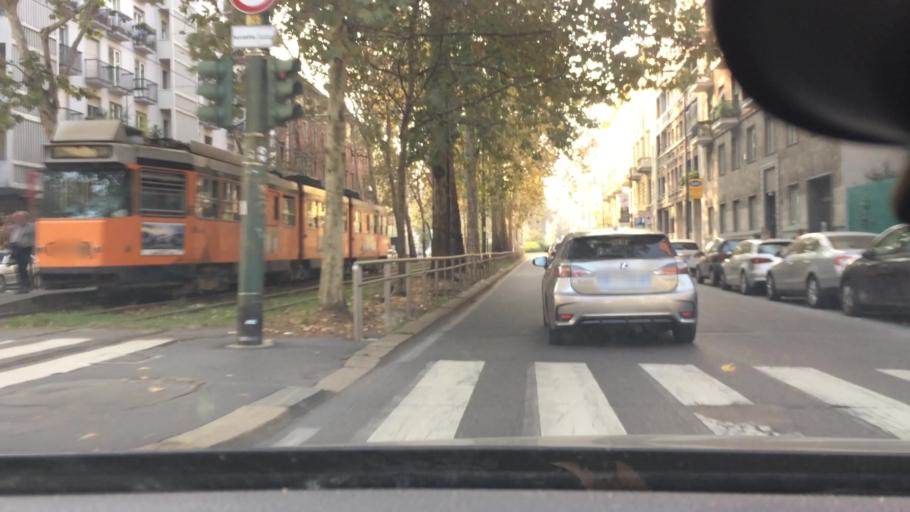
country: IT
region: Lombardy
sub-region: Citta metropolitana di Milano
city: Milano
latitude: 45.4877
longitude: 9.1686
